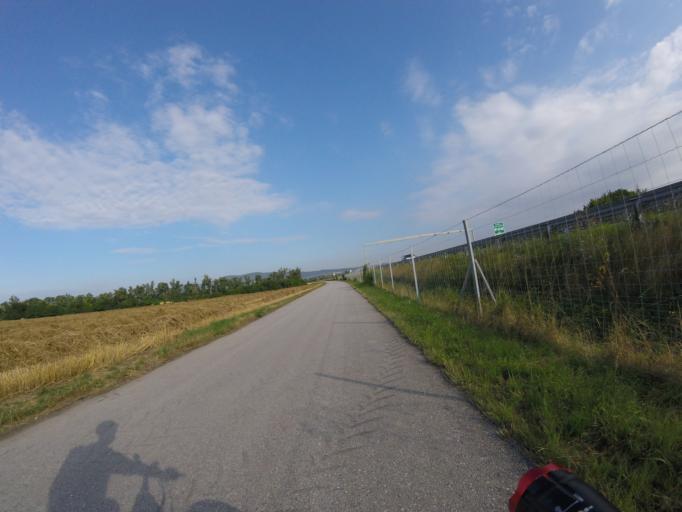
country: AT
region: Lower Austria
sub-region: Politischer Bezirk Baden
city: Trumau
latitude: 48.0240
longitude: 16.3509
